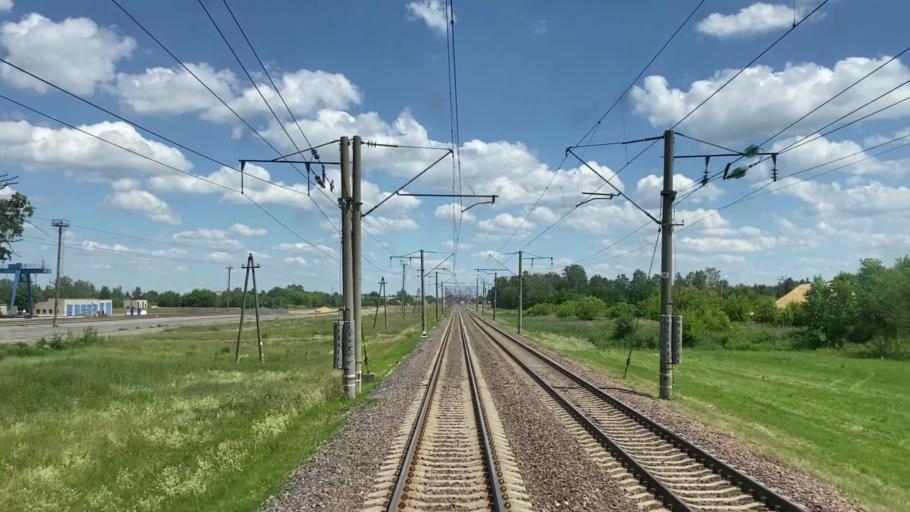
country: BY
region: Brest
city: Ivatsevichy
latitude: 52.6981
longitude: 25.3199
